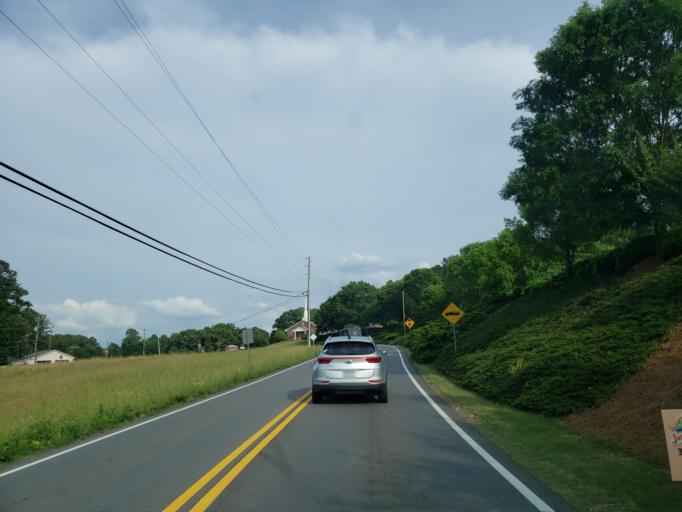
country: US
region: Georgia
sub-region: Fulton County
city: Milton
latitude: 34.1737
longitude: -84.3824
